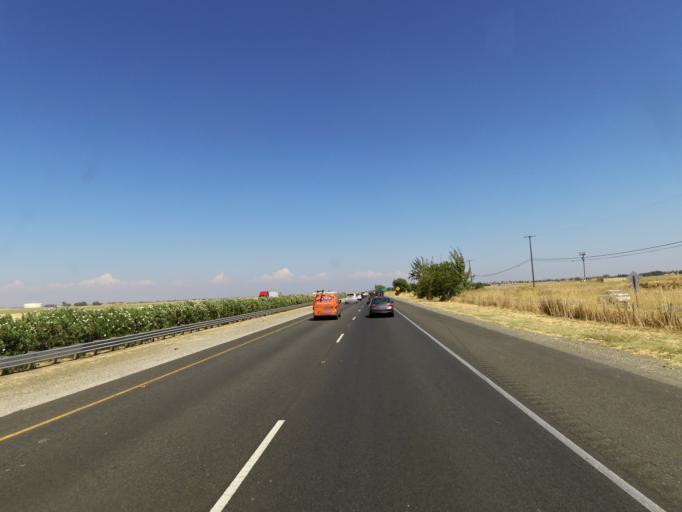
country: US
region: California
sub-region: Yolo County
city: West Sacramento
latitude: 38.6711
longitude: -121.5733
